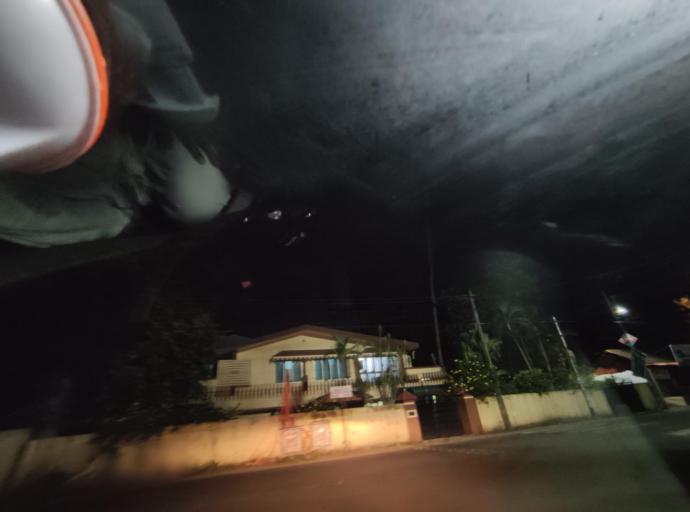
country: IN
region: Kerala
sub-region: Alappuzha
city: Shertallai
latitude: 9.6850
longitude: 76.3518
